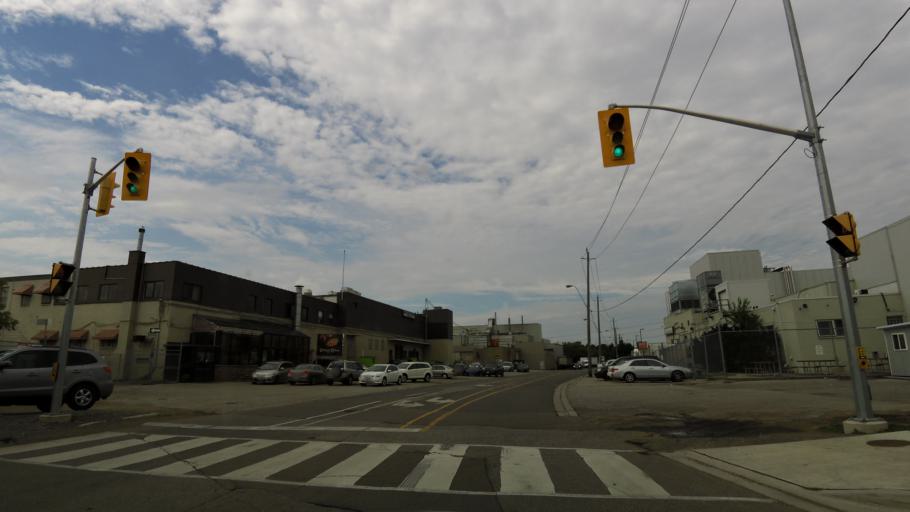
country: CA
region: Ontario
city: Toronto
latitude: 43.6731
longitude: -79.4722
